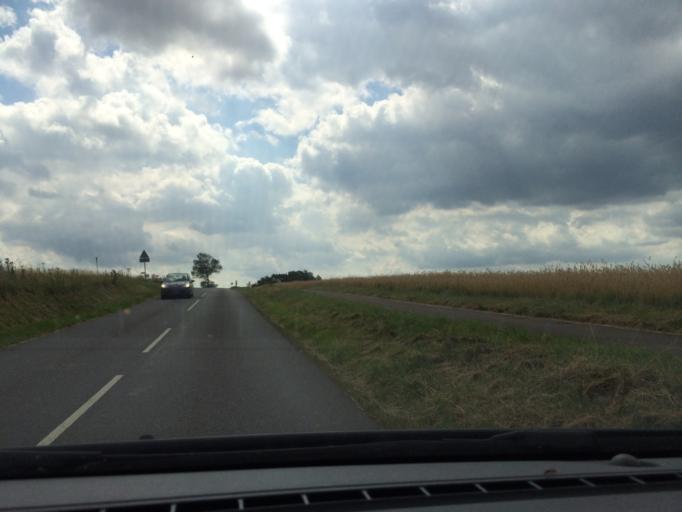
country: DK
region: Zealand
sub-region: Vordingborg Kommune
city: Stege
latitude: 55.0283
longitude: 12.2920
